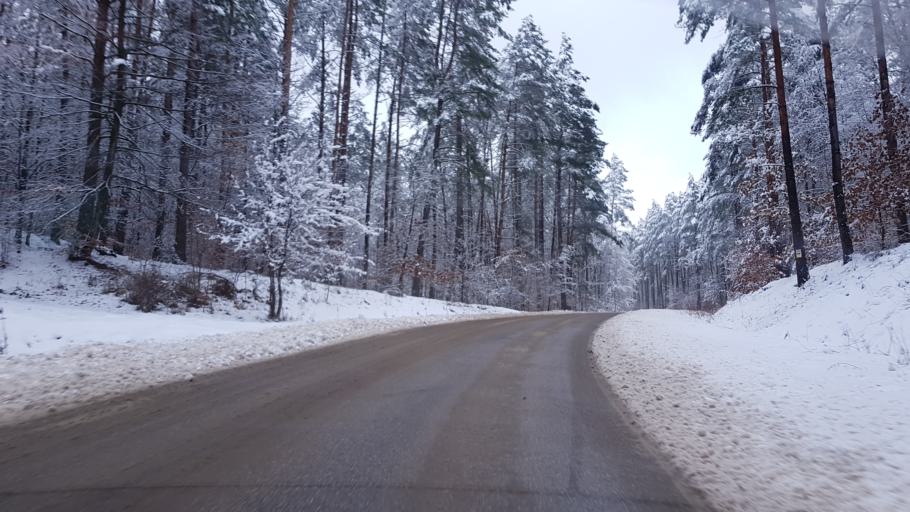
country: PL
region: West Pomeranian Voivodeship
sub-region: Powiat drawski
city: Zlocieniec
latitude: 53.5101
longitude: 16.0026
